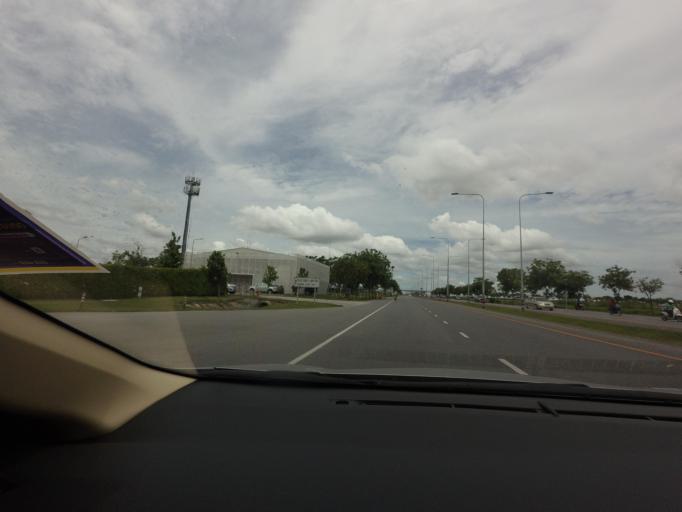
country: TH
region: Bangkok
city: Lat Krabang
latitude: 13.7111
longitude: 100.7755
